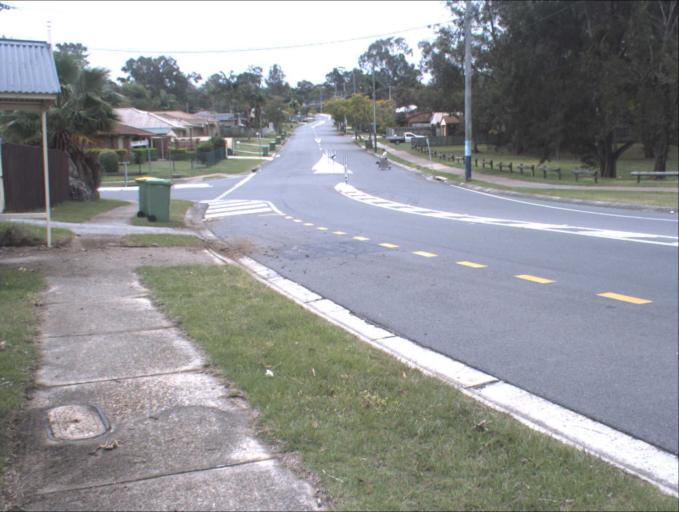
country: AU
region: Queensland
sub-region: Logan
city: Park Ridge South
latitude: -27.6912
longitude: 153.0173
